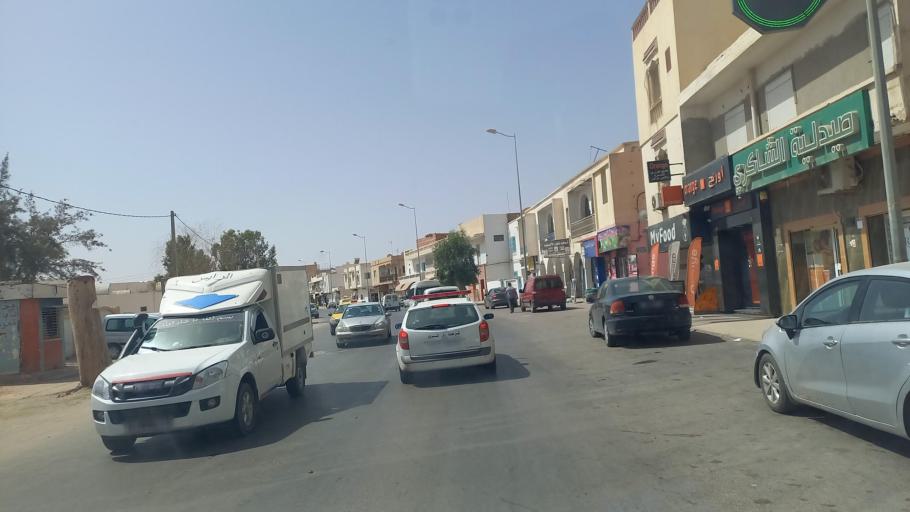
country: TN
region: Madanin
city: Medenine
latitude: 33.3369
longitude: 10.4858
